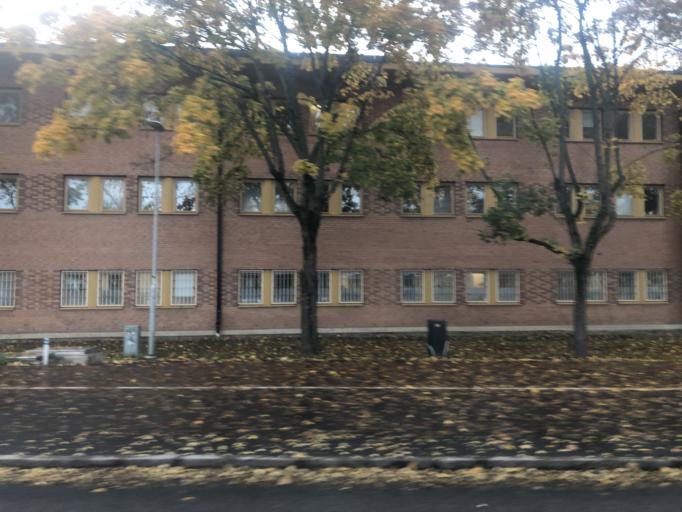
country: SE
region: Stockholm
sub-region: Jarfalla Kommun
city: Jakobsberg
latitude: 59.4212
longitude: 17.8314
